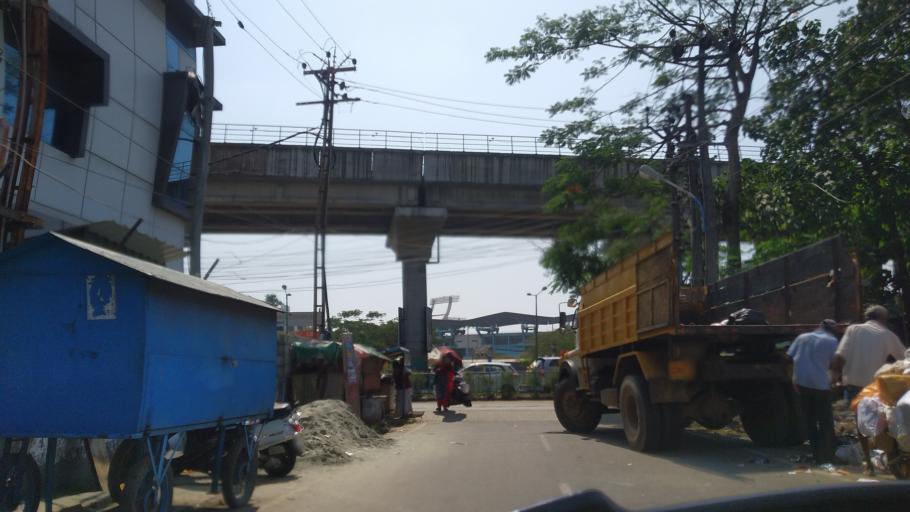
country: IN
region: Kerala
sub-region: Ernakulam
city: Elur
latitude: 10.0014
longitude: 76.2998
